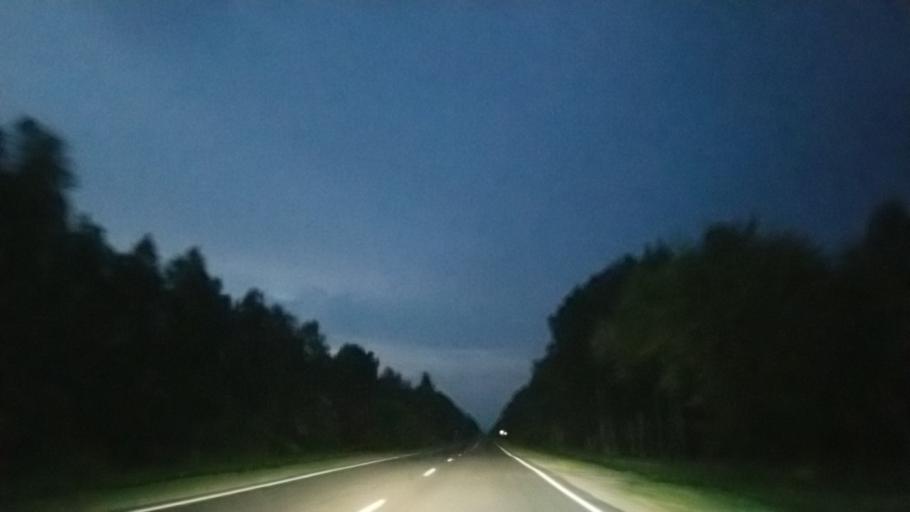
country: PL
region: Lublin Voivodeship
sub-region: Powiat bialski
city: Koden
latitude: 51.8957
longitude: 23.6518
